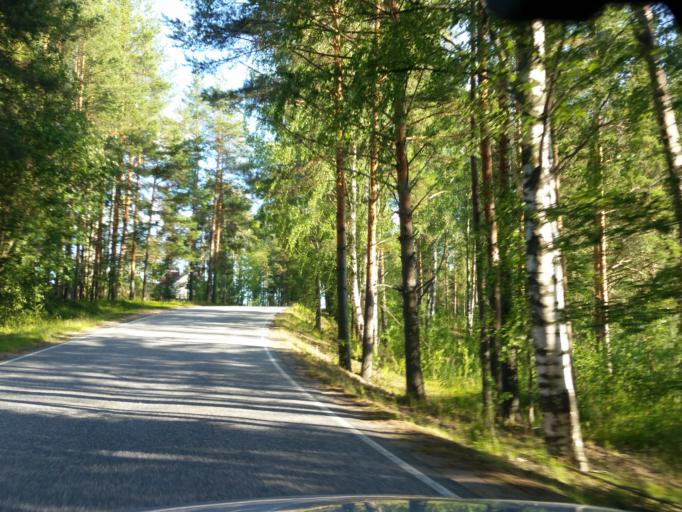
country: FI
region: Southern Savonia
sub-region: Savonlinna
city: Sulkava
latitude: 61.7706
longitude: 28.4337
